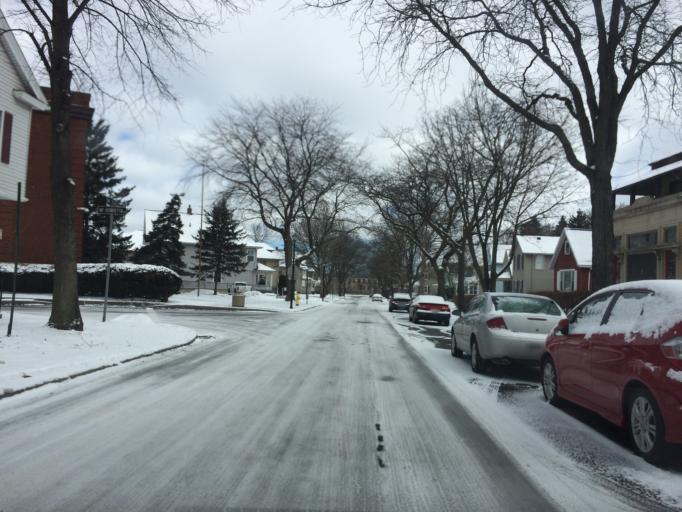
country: US
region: New York
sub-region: Monroe County
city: Rochester
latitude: 43.1398
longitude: -77.5879
